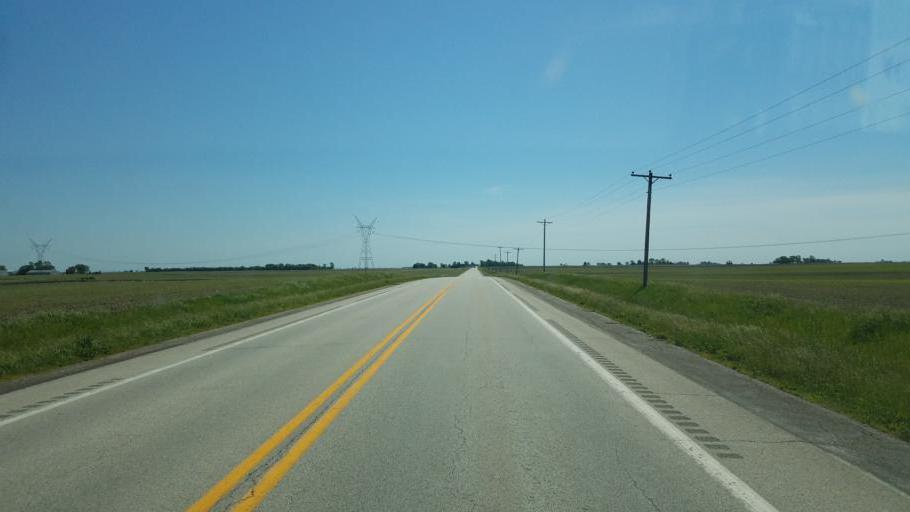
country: US
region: Illinois
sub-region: McLean County
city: Heyworth
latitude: 40.3123
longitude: -88.9378
